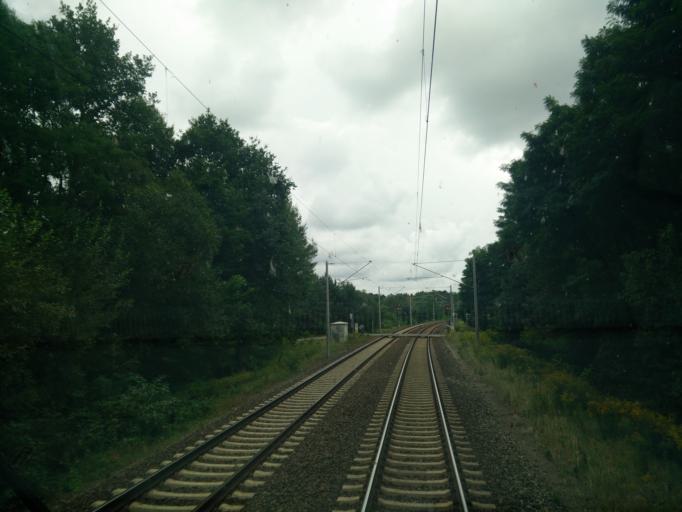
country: DE
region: Brandenburg
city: Gross Koris
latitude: 52.1696
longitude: 13.6463
